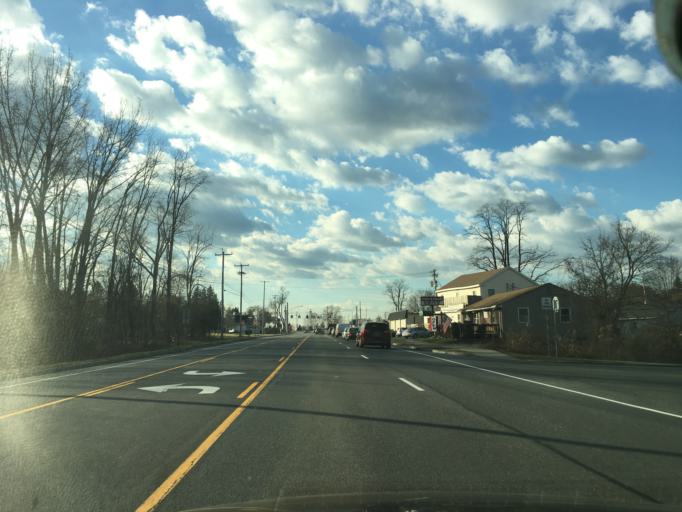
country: US
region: New York
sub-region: Rensselaer County
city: Hampton Manor
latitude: 42.6522
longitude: -73.6955
